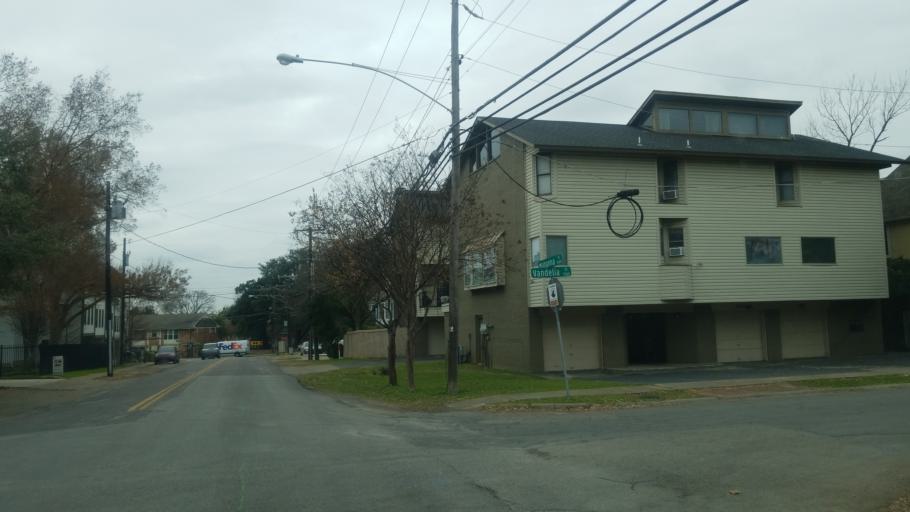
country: US
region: Texas
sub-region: Dallas County
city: Highland Park
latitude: 32.8217
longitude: -96.8219
